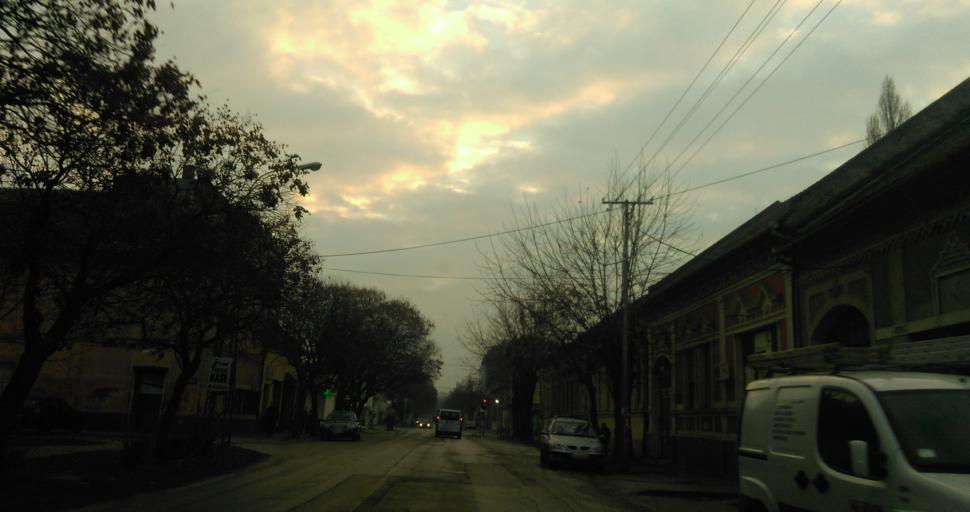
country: RS
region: Autonomna Pokrajina Vojvodina
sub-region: Juznobacki Okrug
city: Becej
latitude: 45.6183
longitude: 20.0440
